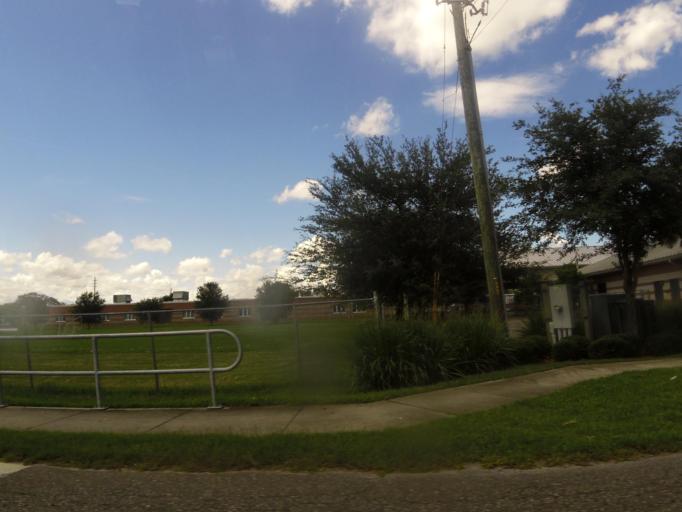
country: US
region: Florida
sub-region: Nassau County
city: Fernandina Beach
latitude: 30.6552
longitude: -81.4572
